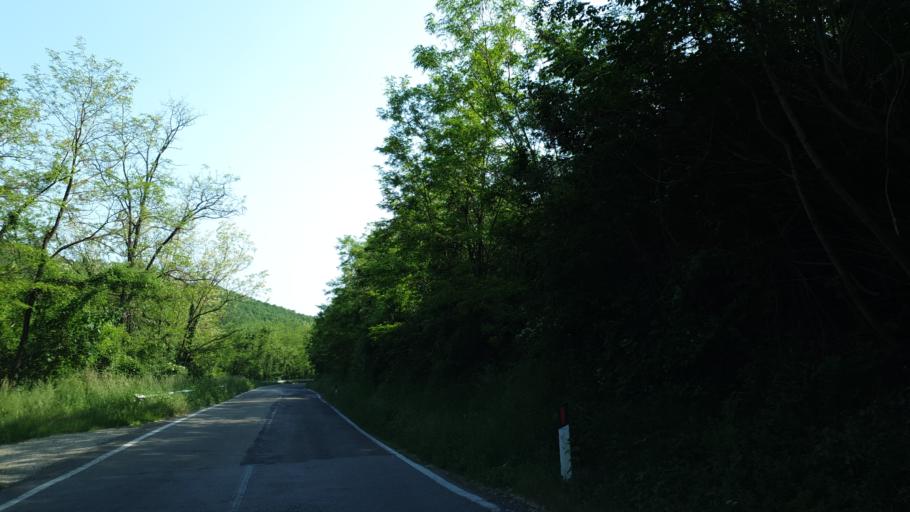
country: IT
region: Tuscany
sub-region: Province of Arezzo
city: Soci
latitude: 43.7584
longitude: 11.8302
